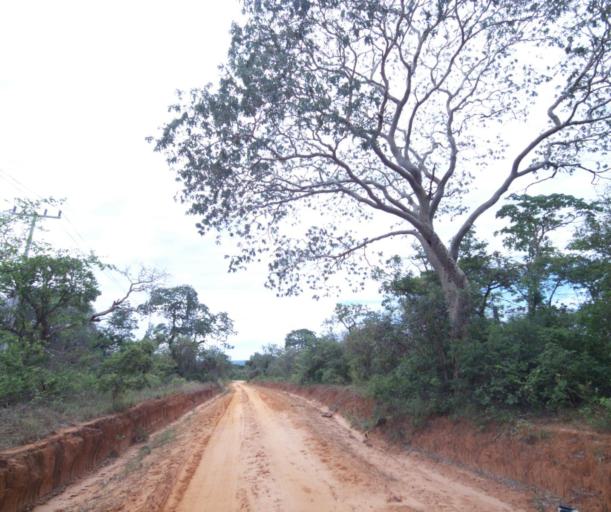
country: BR
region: Bahia
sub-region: Carinhanha
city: Carinhanha
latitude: -14.2459
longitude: -44.3784
